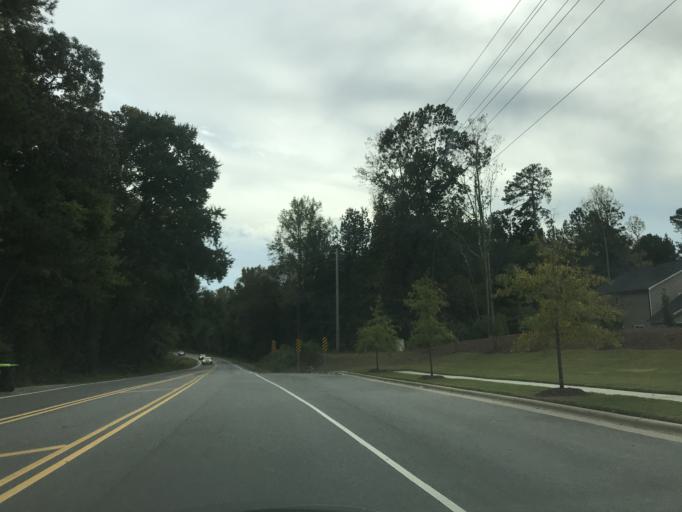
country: US
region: North Carolina
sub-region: Wake County
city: Rolesville
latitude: 35.9021
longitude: -78.5066
